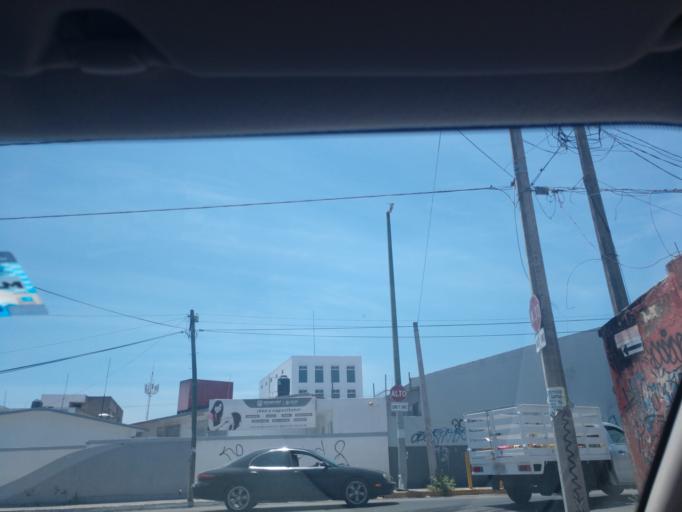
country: MX
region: Nayarit
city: Tepic
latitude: 21.5161
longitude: -104.8983
